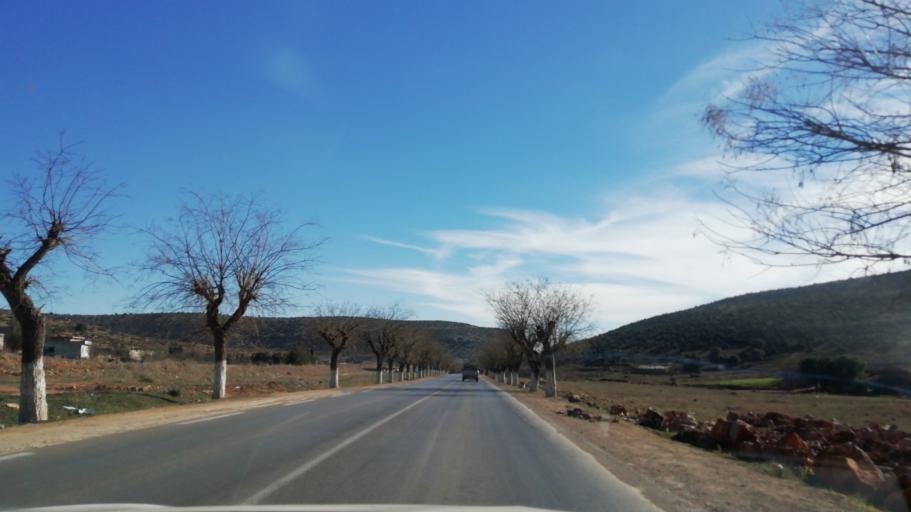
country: DZ
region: Tlemcen
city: Sebdou
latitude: 34.7064
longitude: -1.3190
